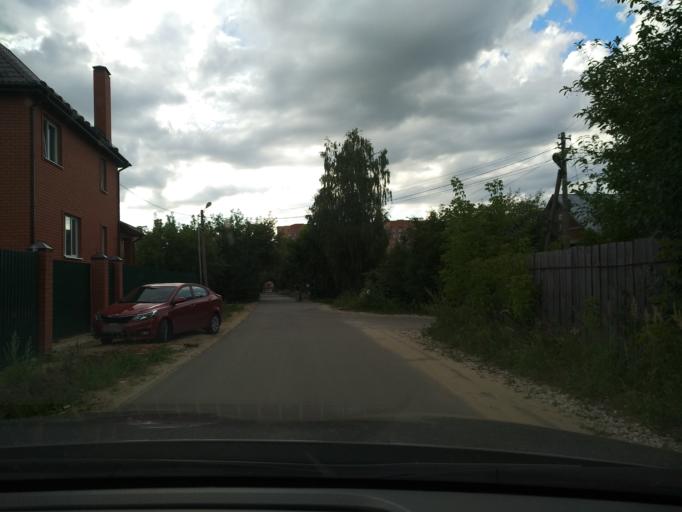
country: RU
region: Moskovskaya
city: Yegor'yevsk
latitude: 55.3674
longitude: 39.0841
